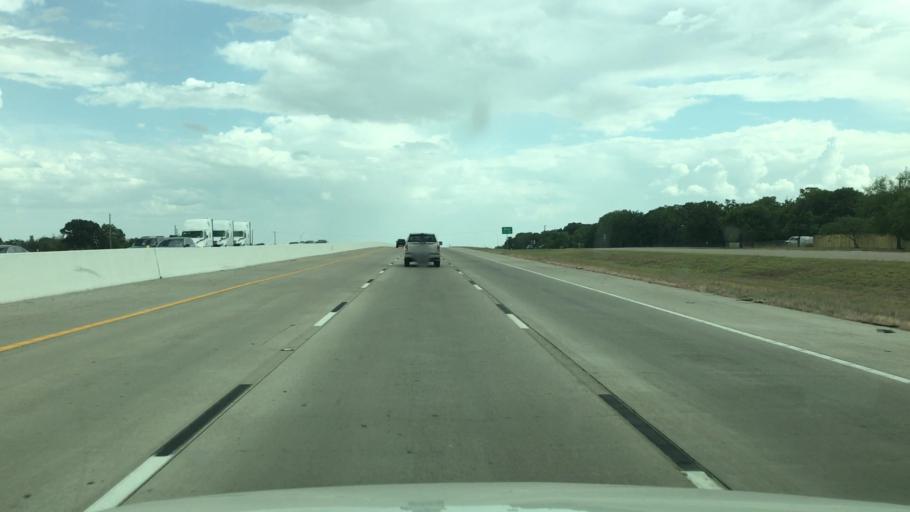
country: US
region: Texas
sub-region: McLennan County
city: West
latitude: 31.7400
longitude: -97.1037
